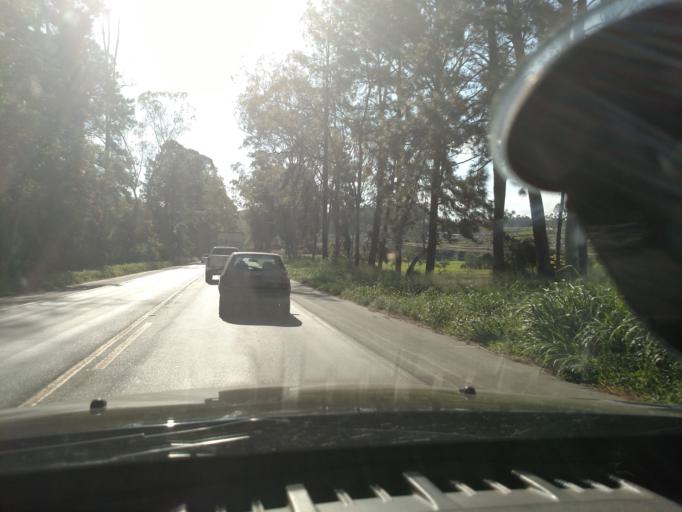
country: BR
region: Santa Catarina
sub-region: Rio Do Sul
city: Rio do Sul
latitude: -27.2661
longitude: -49.8778
